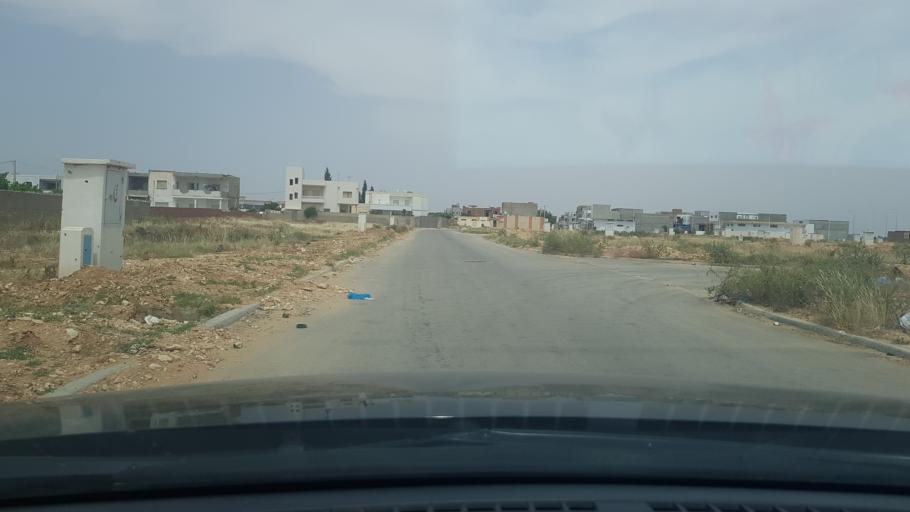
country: TN
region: Safaqis
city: Al Qarmadah
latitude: 34.8223
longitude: 10.7428
